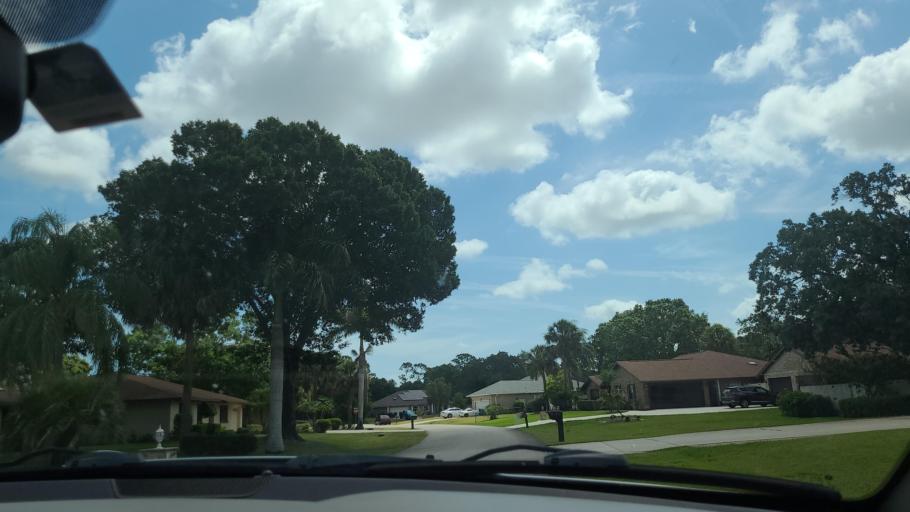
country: US
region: Florida
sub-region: Brevard County
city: West Melbourne
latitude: 28.0244
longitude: -80.6517
